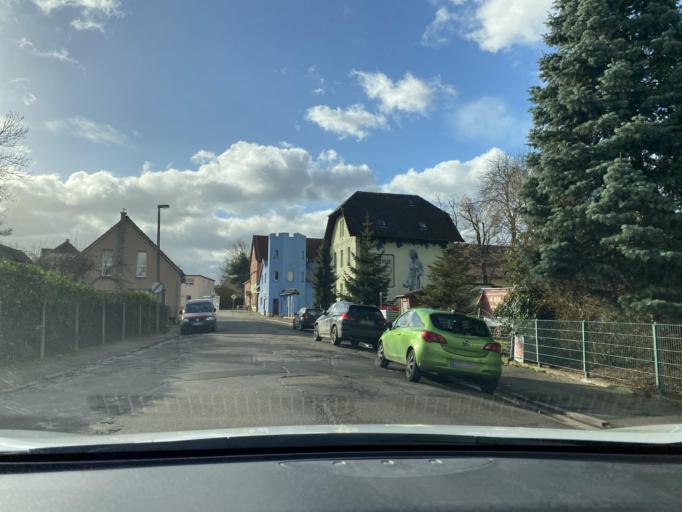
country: DE
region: Saxony
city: Zwenkau
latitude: 51.2662
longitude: 12.3090
